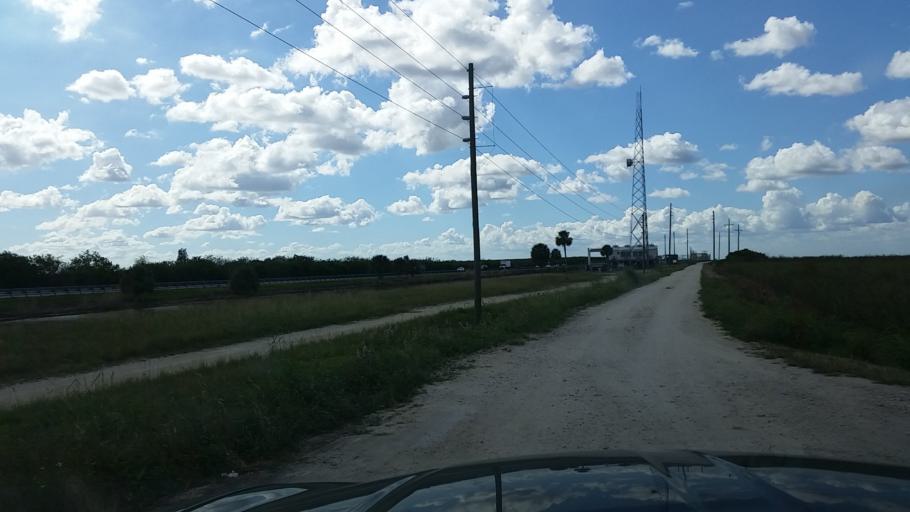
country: US
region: Florida
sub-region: Miami-Dade County
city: Kendall West
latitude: 25.7616
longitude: -80.4990
